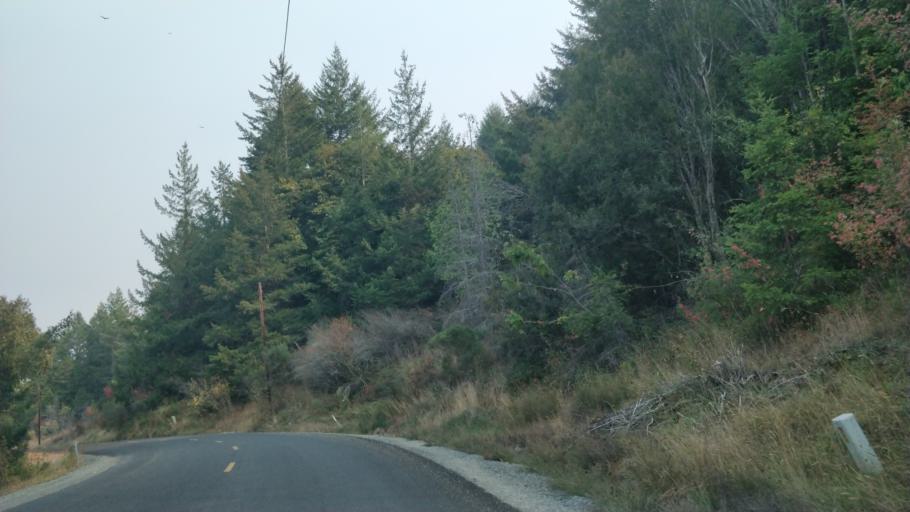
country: US
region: California
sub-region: Humboldt County
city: Rio Dell
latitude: 40.2520
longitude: -124.1863
